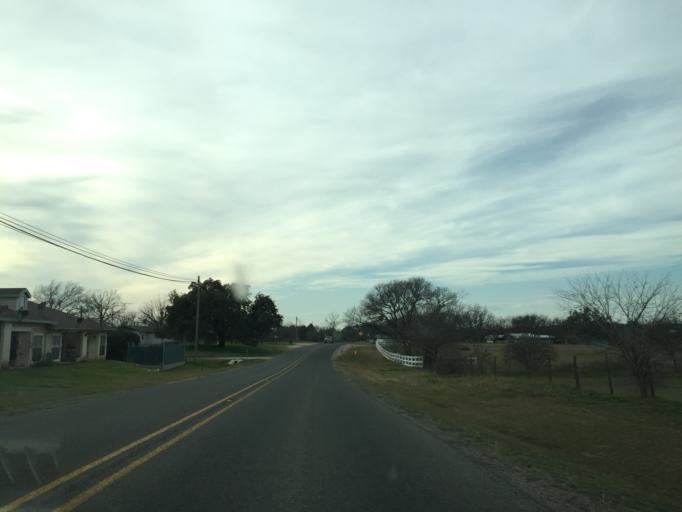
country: US
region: Texas
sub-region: Llano County
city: Llano
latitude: 30.7517
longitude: -98.6975
